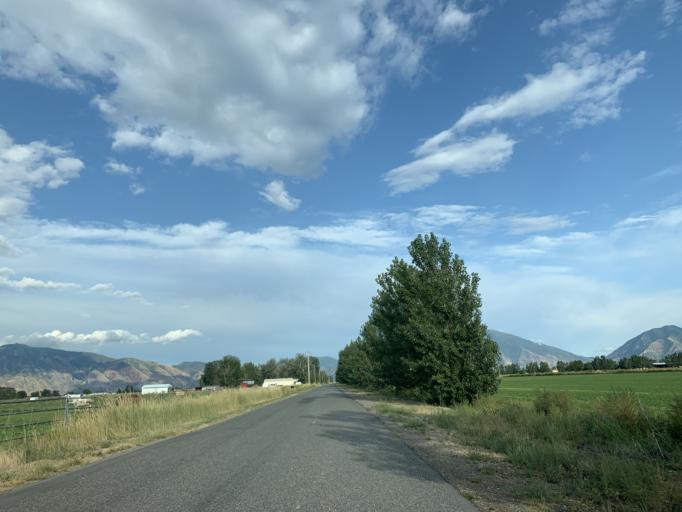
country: US
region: Utah
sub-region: Utah County
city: Benjamin
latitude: 40.1291
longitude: -111.7487
